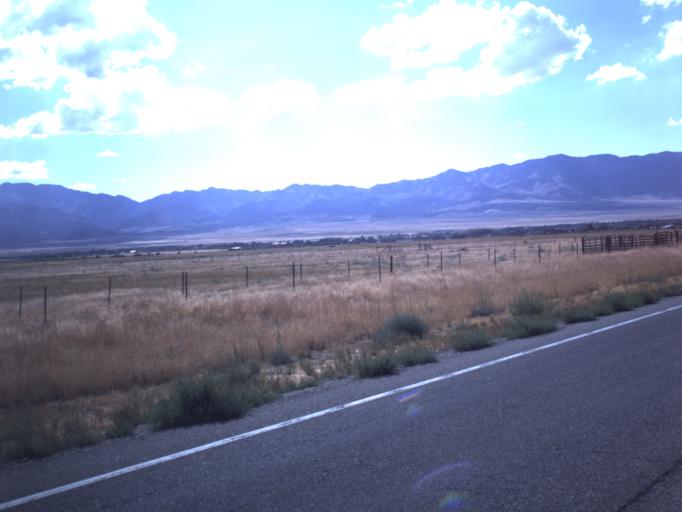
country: US
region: Utah
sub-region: Tooele County
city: Grantsville
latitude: 40.5828
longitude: -112.4034
